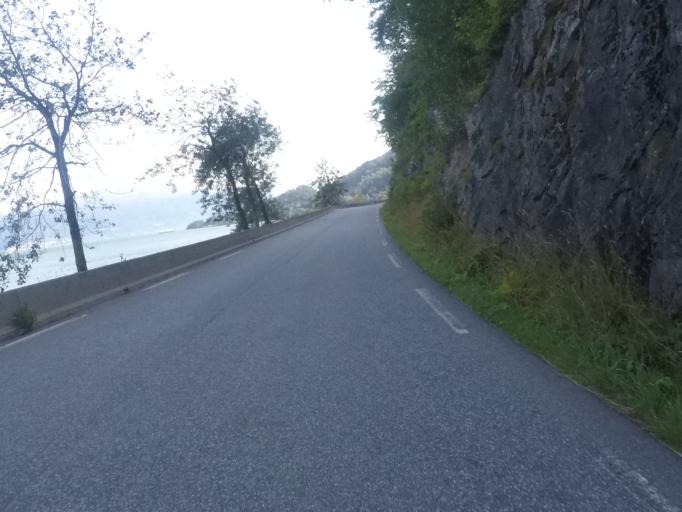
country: NO
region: Sogn og Fjordane
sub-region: Balestrand
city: Balestrand
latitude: 61.2373
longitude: 6.5516
